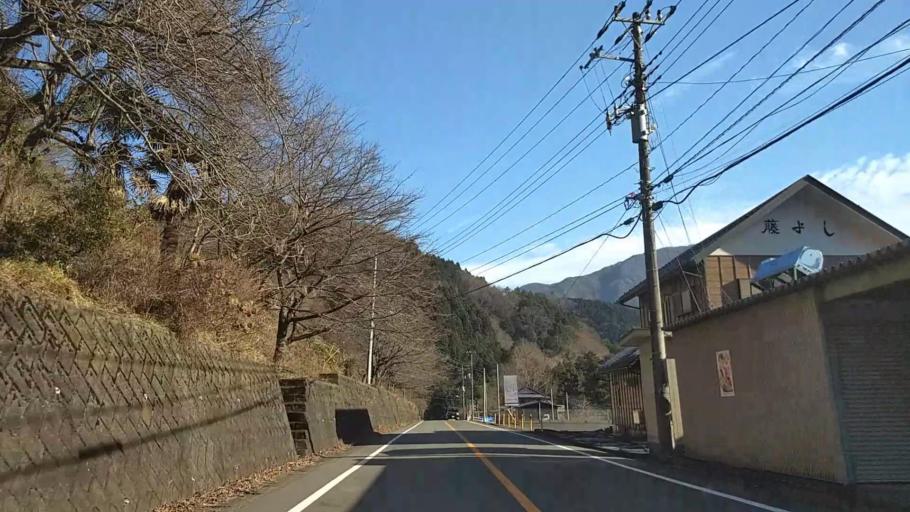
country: JP
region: Yamanashi
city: Uenohara
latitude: 35.5352
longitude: 139.0903
